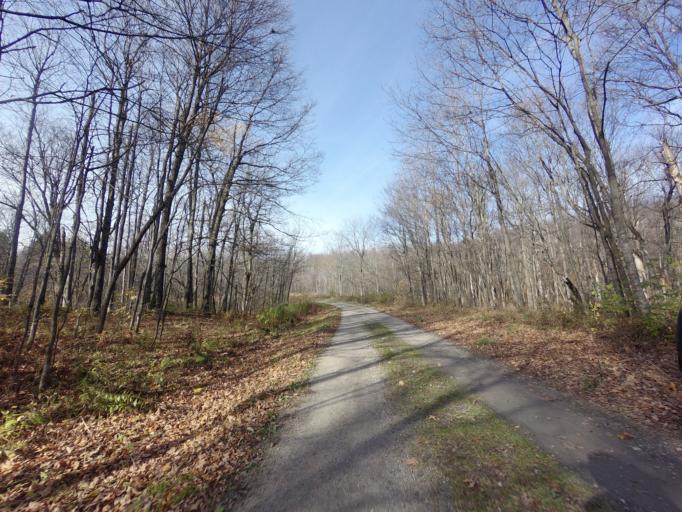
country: CA
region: Quebec
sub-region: Outaouais
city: Wakefield
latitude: 45.5185
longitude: -75.9110
